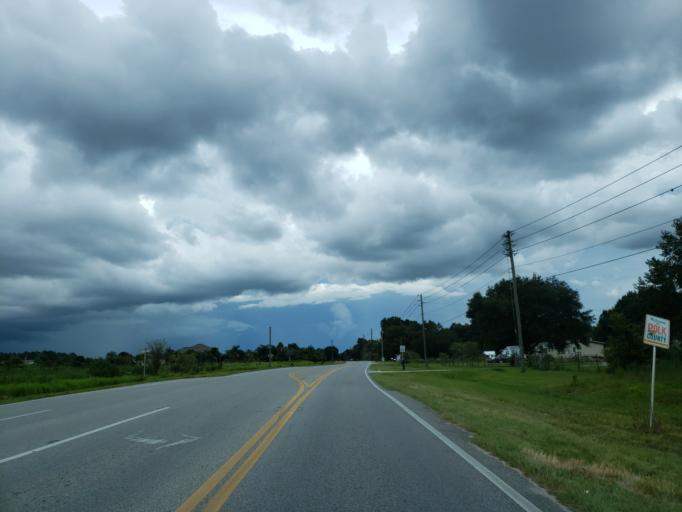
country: US
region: Florida
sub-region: Polk County
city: Willow Oak
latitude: 27.9528
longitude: -82.0550
